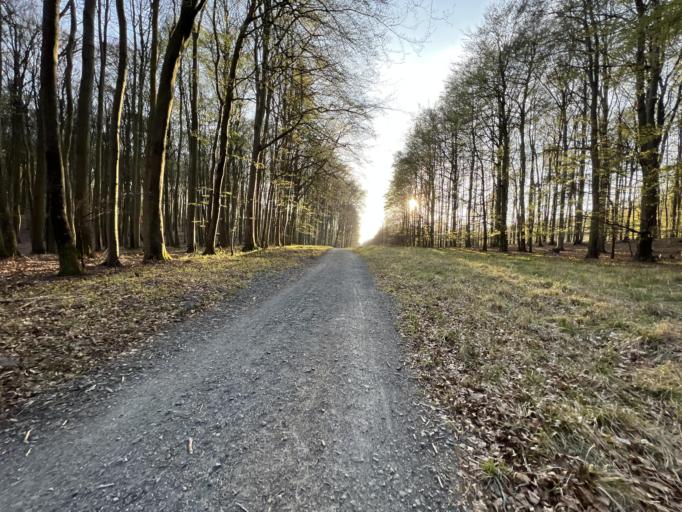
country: DE
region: Mecklenburg-Vorpommern
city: Sassnitz
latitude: 54.5361
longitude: 13.6600
